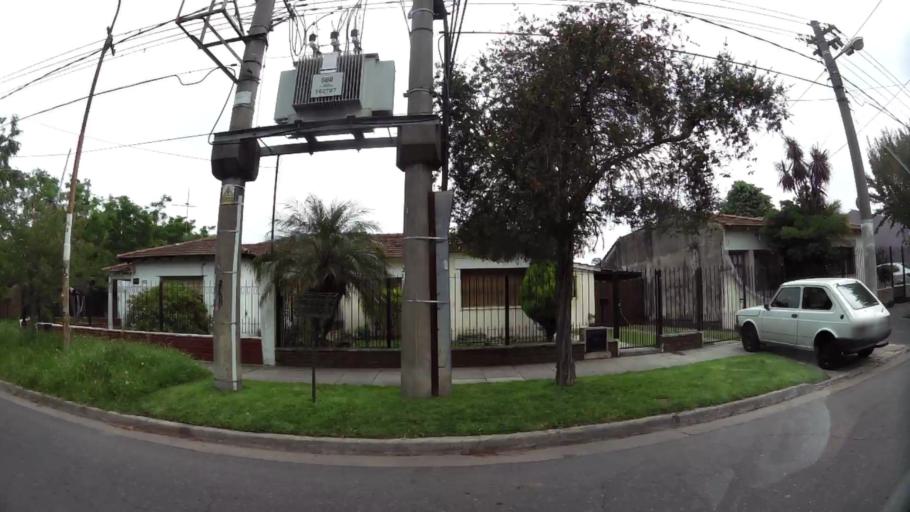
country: AR
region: Buenos Aires
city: San Justo
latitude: -34.7337
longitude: -58.5310
